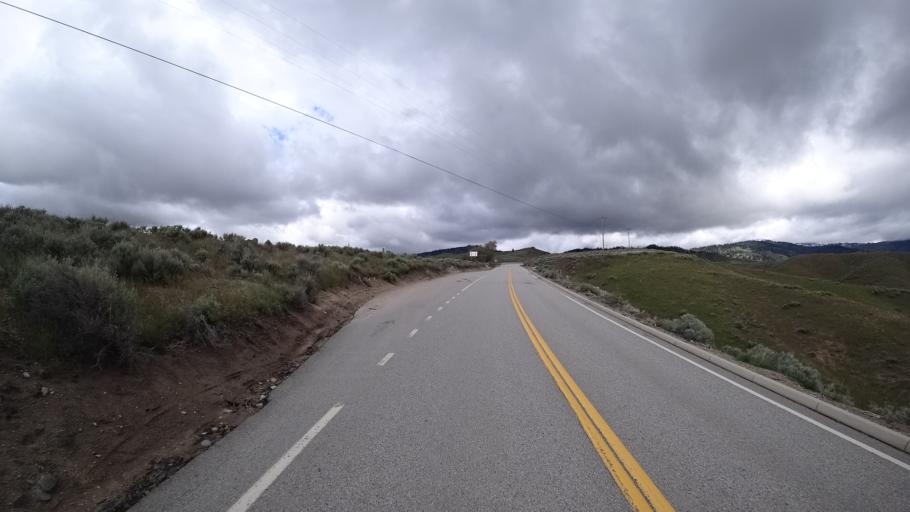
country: US
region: Idaho
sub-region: Ada County
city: Boise
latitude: 43.7066
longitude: -116.1656
